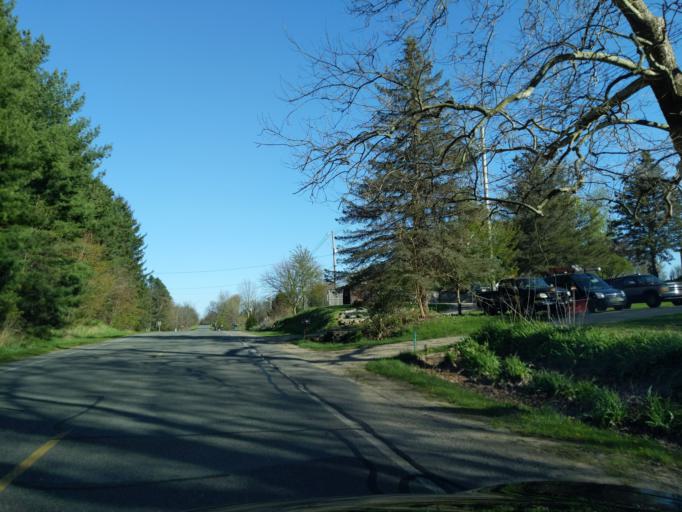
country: US
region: Michigan
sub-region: Ionia County
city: Portland
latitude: 42.8255
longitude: -84.8431
